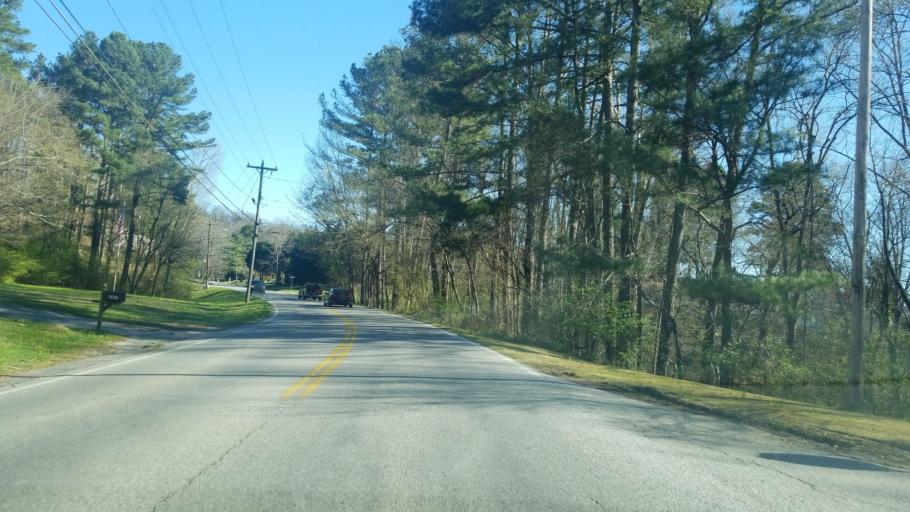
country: US
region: Tennessee
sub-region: Hamilton County
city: East Chattanooga
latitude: 35.1151
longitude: -85.2121
